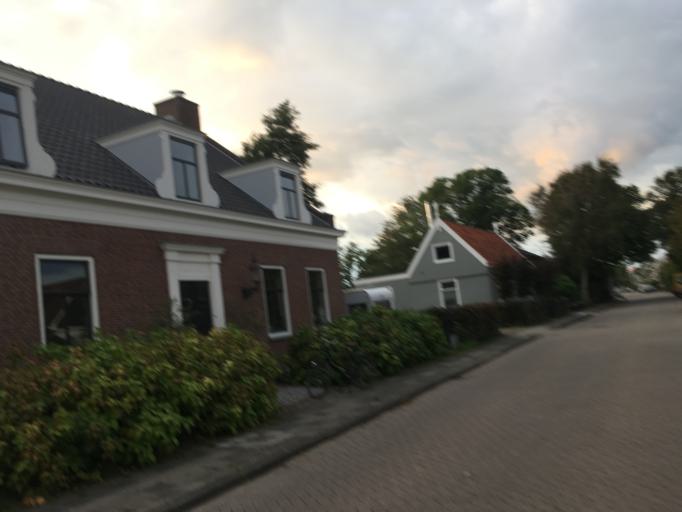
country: NL
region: North Holland
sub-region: Gemeente Zaanstad
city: Zaanstad
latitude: 52.4563
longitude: 4.7746
